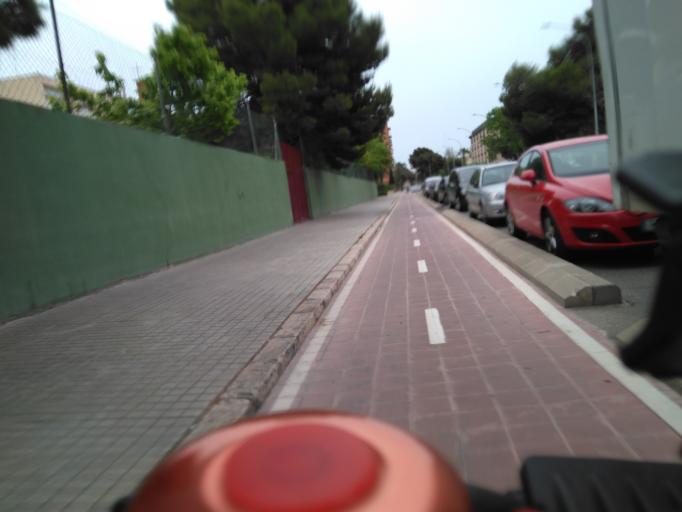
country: ES
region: Valencia
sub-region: Provincia de Valencia
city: Mislata
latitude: 39.4667
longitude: -0.4029
